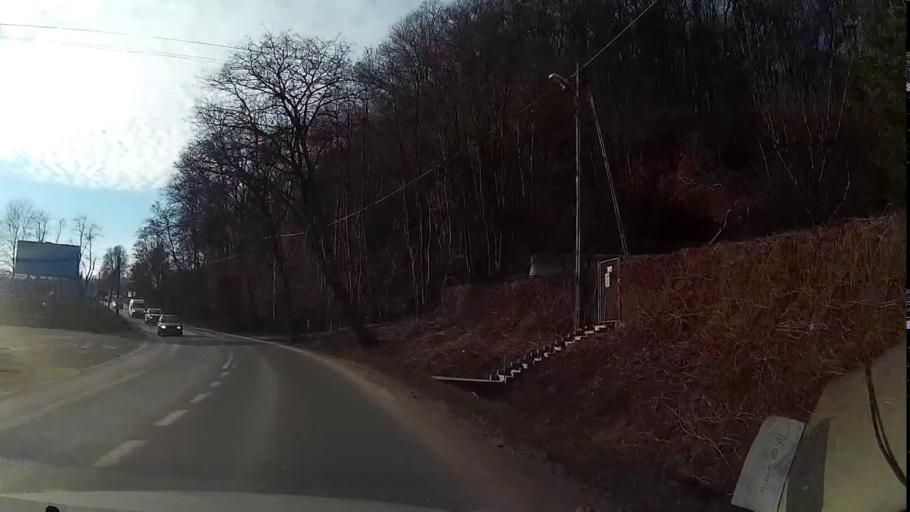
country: PL
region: Lesser Poland Voivodeship
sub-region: Powiat krakowski
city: Kryspinow
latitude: 50.0440
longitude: 19.8473
